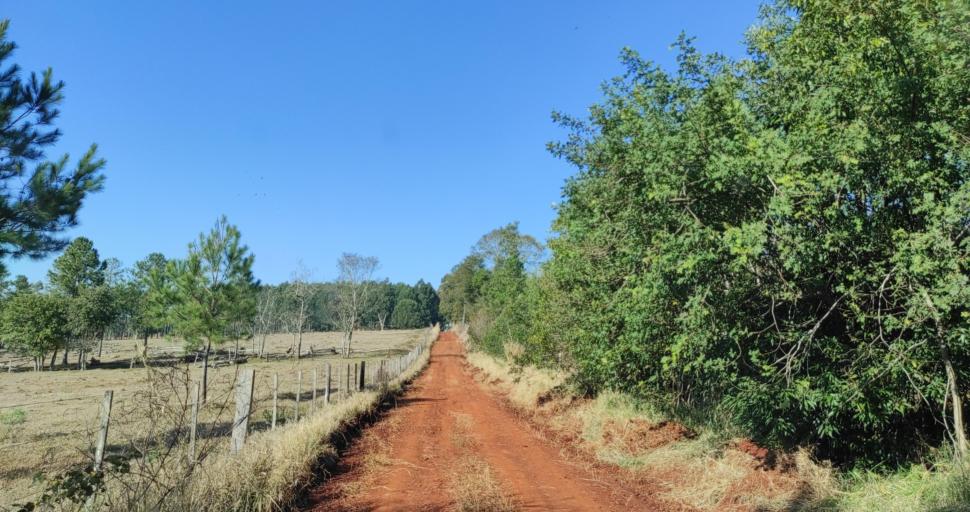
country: AR
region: Misiones
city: Capiovi
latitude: -26.8747
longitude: -55.0365
